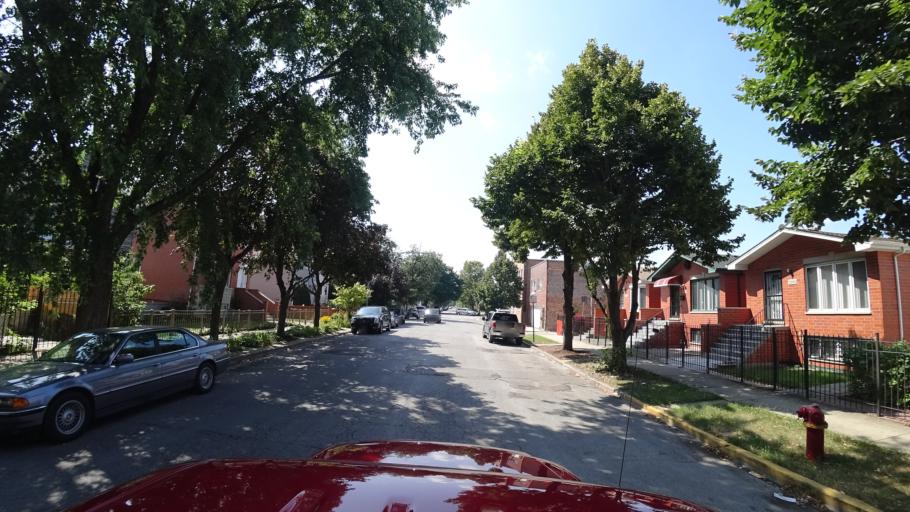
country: US
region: Illinois
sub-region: Cook County
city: Chicago
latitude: 41.8238
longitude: -87.6874
